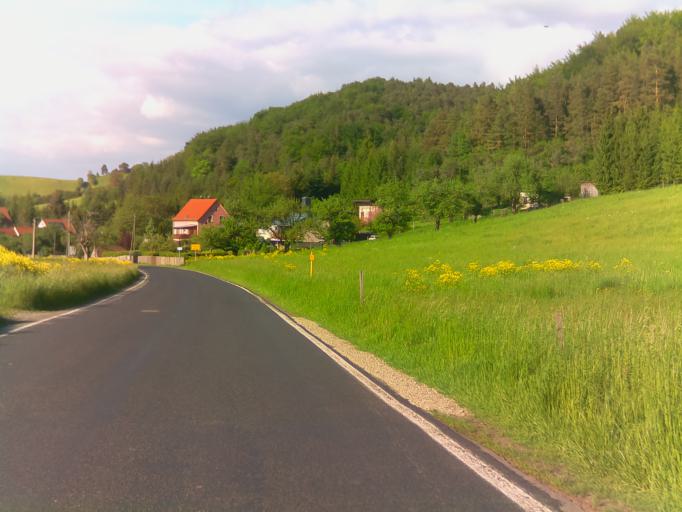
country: DE
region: Thuringia
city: Allendorf
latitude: 50.6505
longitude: 11.1569
